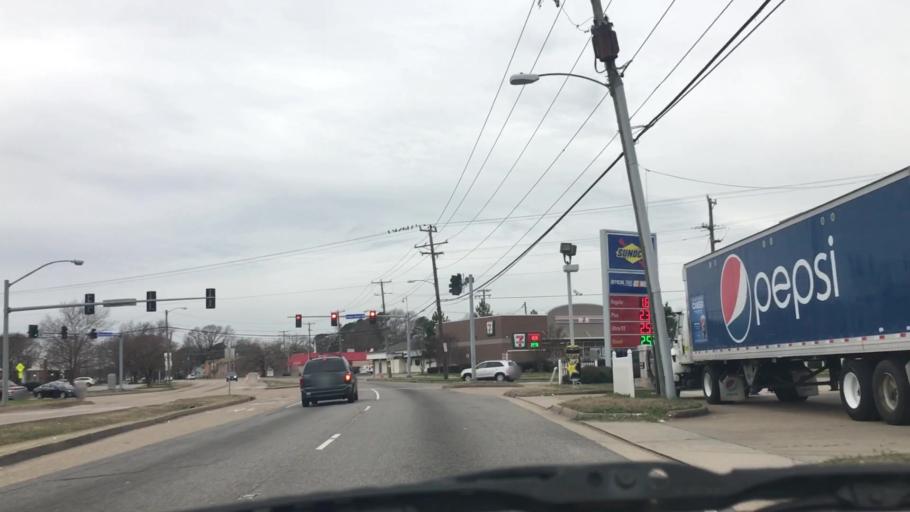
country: US
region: Virginia
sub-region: City of Norfolk
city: Norfolk
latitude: 36.8670
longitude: -76.2340
